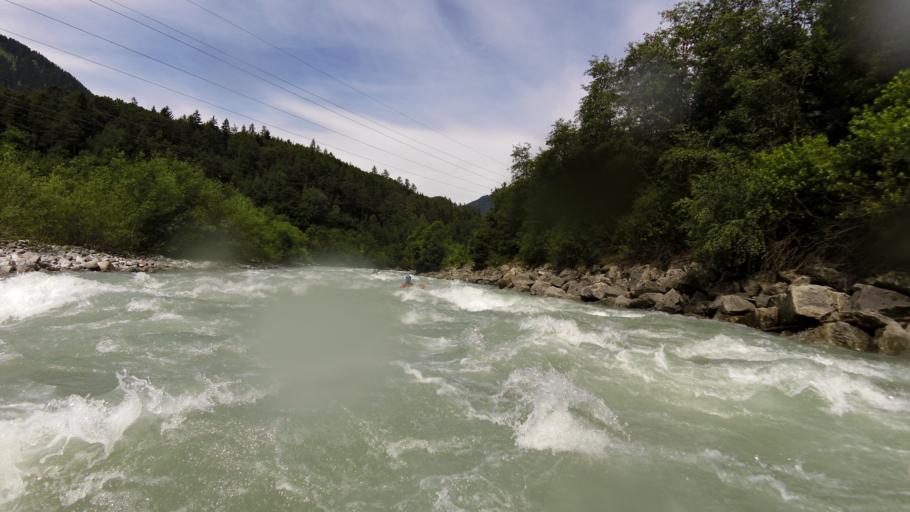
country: AT
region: Tyrol
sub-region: Politischer Bezirk Imst
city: Sautens
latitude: 47.2163
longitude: 10.8617
